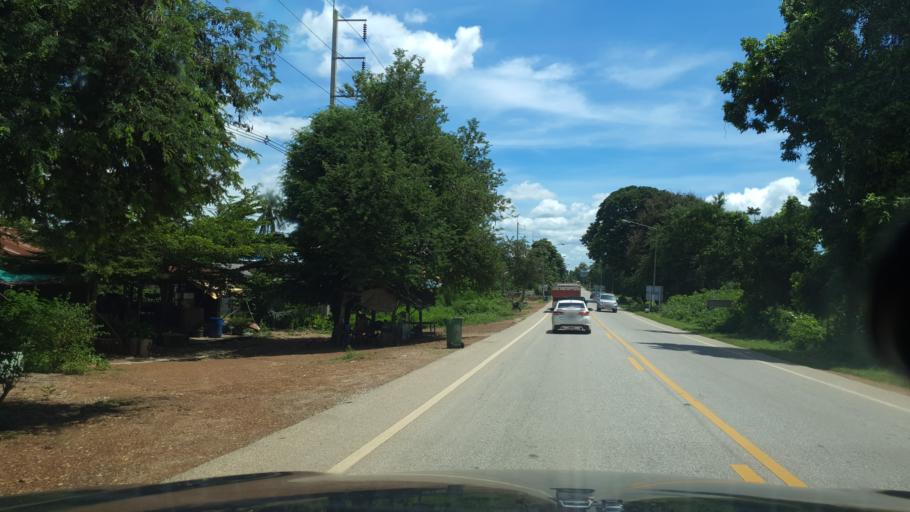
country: TH
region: Sukhothai
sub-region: Amphoe Si Satchanalai
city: Si Satchanalai
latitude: 17.4374
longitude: 99.8007
